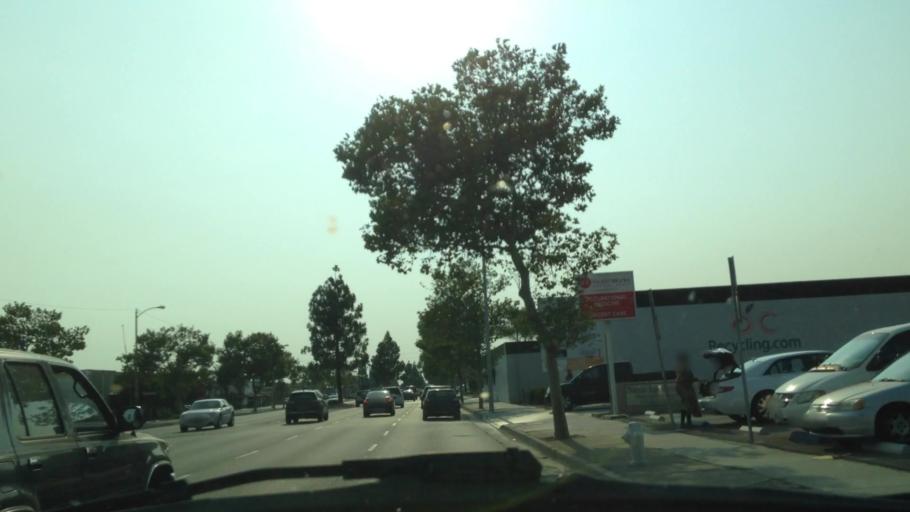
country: US
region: California
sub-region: Orange County
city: Tustin
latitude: 33.7268
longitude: -117.8465
